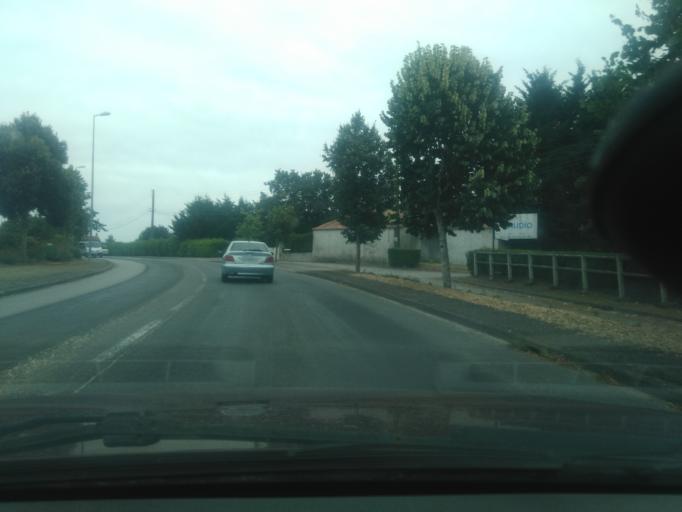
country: FR
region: Poitou-Charentes
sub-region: Departement des Deux-Sevres
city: Parthenay
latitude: 46.6357
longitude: -0.2619
